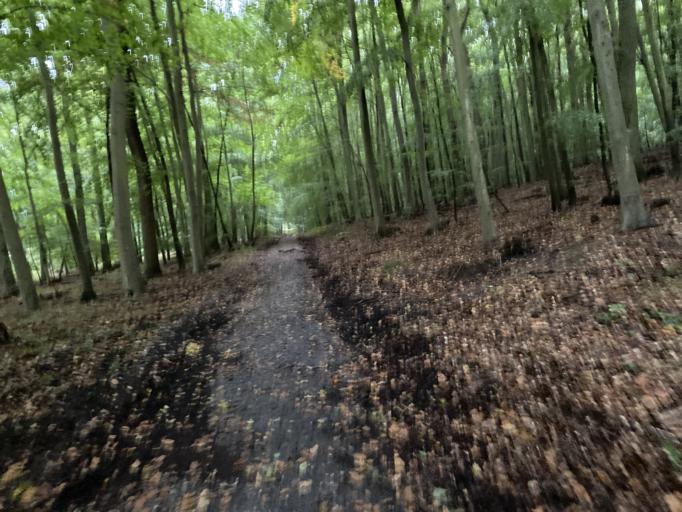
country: DE
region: Mecklenburg-Vorpommern
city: Ostseebad Binz
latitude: 54.4482
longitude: 13.5518
